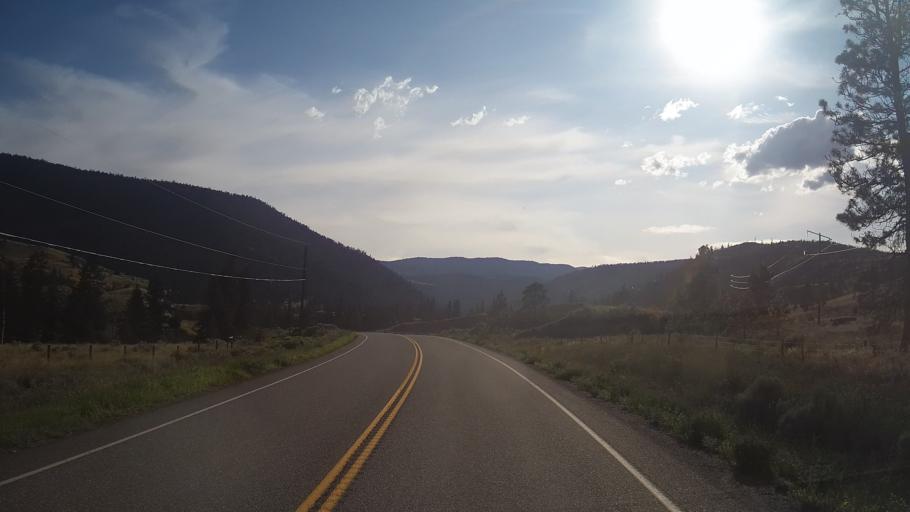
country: CA
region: British Columbia
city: Cache Creek
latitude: 50.8870
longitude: -121.4658
